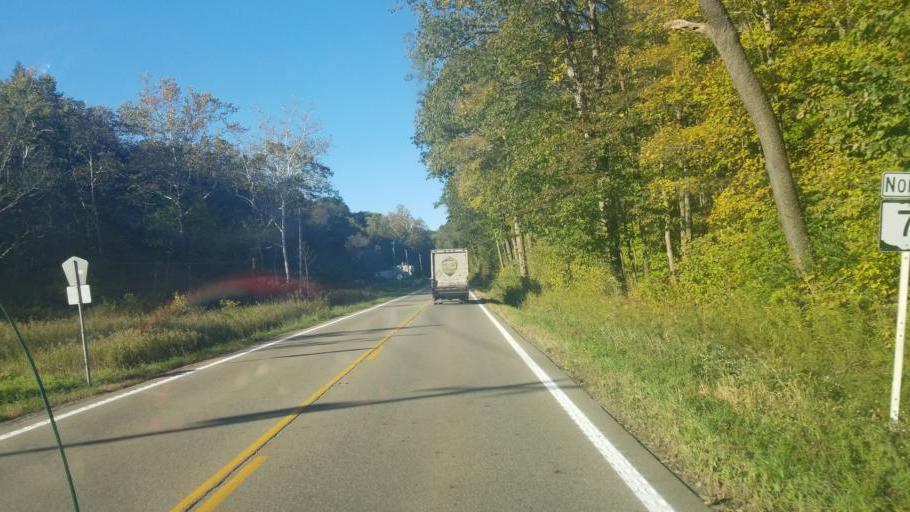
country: US
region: Ohio
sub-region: Columbiana County
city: Glenmoor
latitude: 40.7345
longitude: -80.6385
